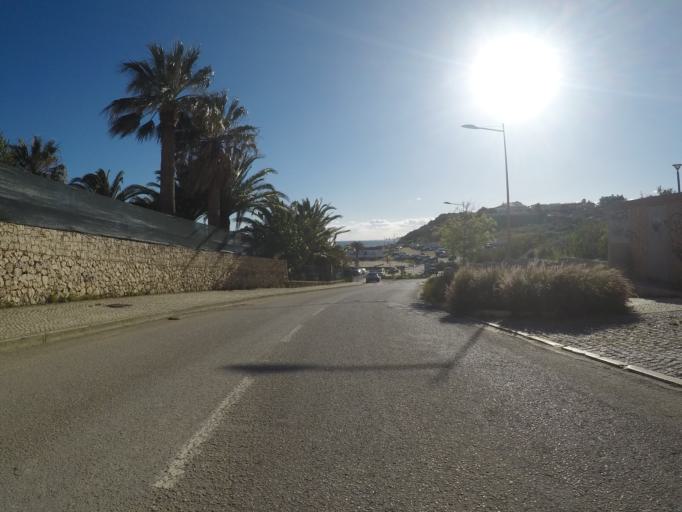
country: PT
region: Faro
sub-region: Lagos
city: Lagos
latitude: 37.0864
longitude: -8.6867
